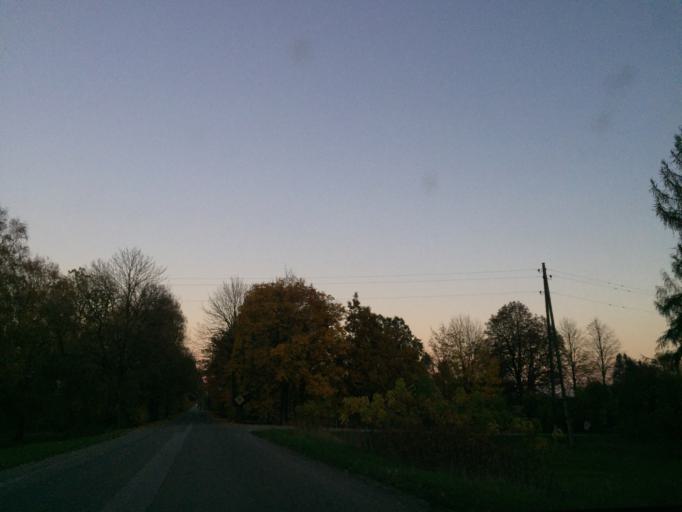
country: LT
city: Akmene
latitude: 56.3820
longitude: 22.6275
